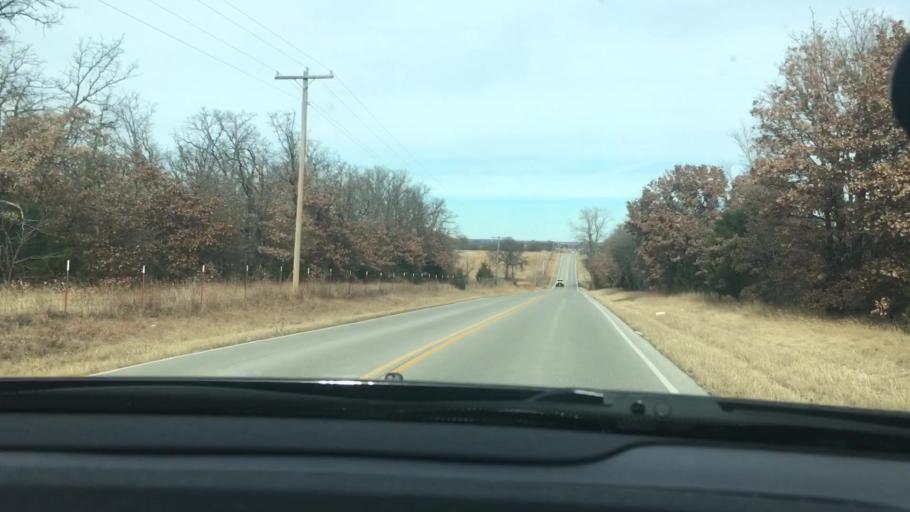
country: US
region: Oklahoma
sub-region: Carter County
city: Ardmore
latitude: 34.1788
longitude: -97.0731
